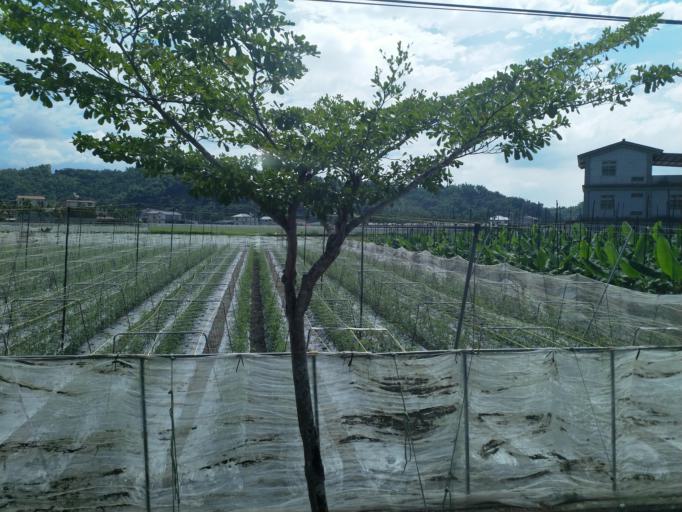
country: TW
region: Taiwan
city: Yujing
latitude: 22.9047
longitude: 120.5564
